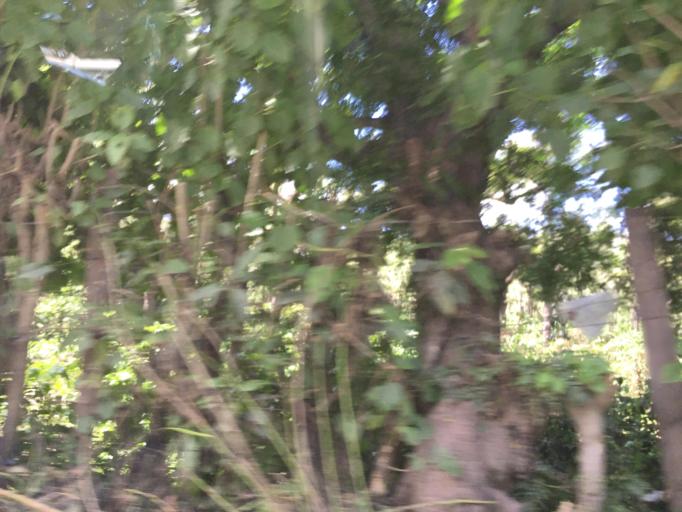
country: GT
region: Sacatepequez
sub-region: Municipio de Santa Maria de Jesus
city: Santa Maria de Jesus
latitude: 14.5380
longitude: -90.7346
